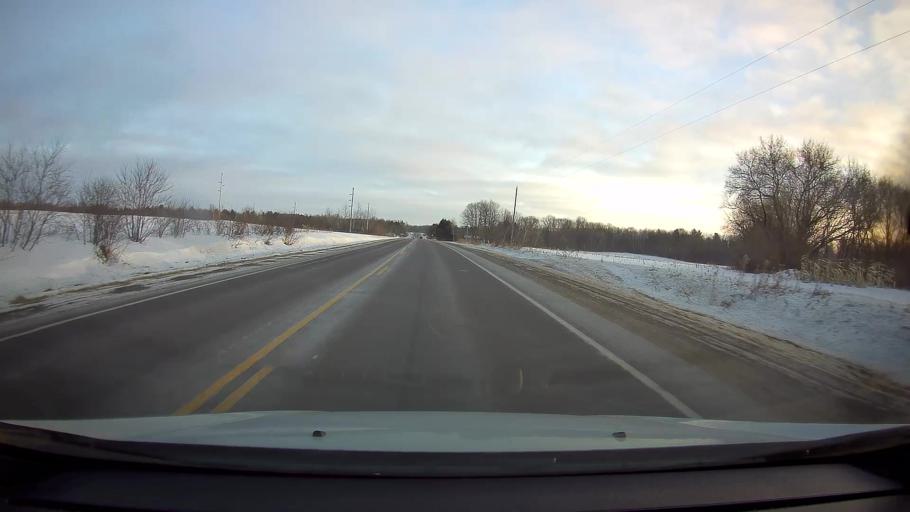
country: US
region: Wisconsin
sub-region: Polk County
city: Clear Lake
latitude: 45.2589
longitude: -92.2627
